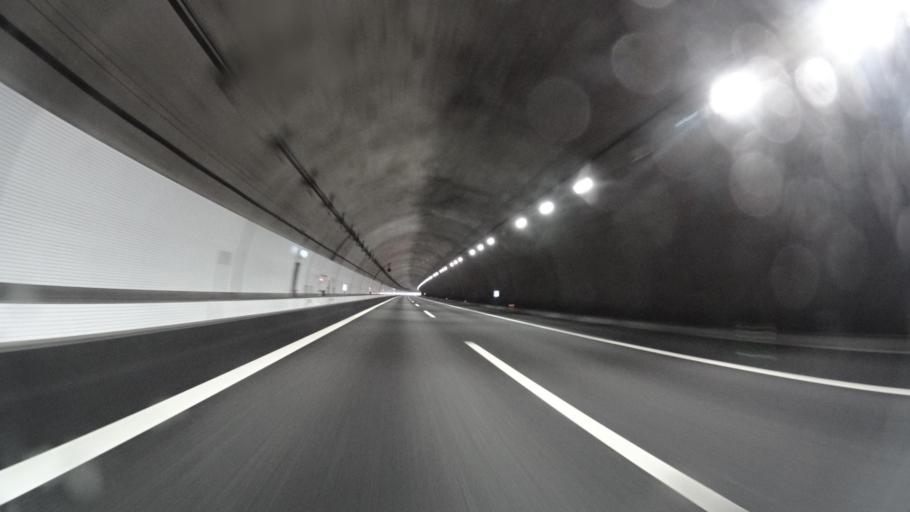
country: JP
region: Shiga Prefecture
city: Minakuchicho-matoba
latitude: 34.9221
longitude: 136.1232
